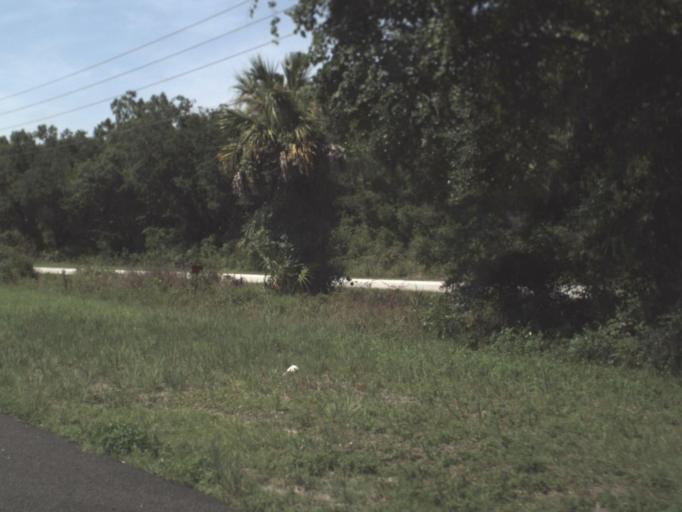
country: US
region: Florida
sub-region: Levy County
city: Inglis
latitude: 28.9941
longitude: -82.6508
